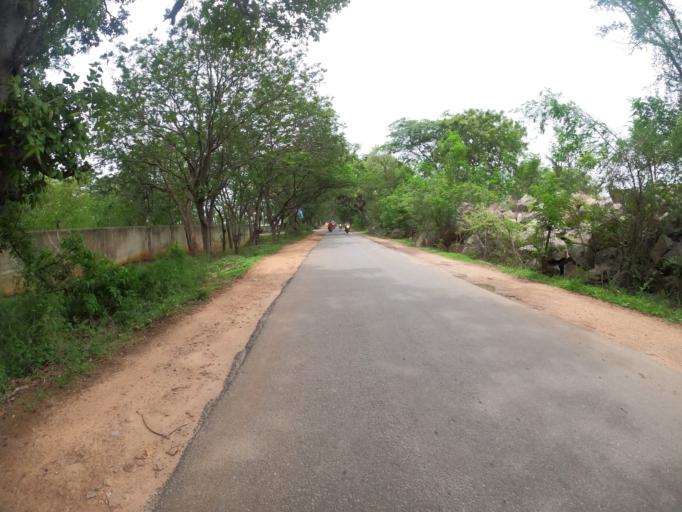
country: IN
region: Telangana
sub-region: Hyderabad
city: Hyderabad
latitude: 17.3452
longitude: 78.3751
